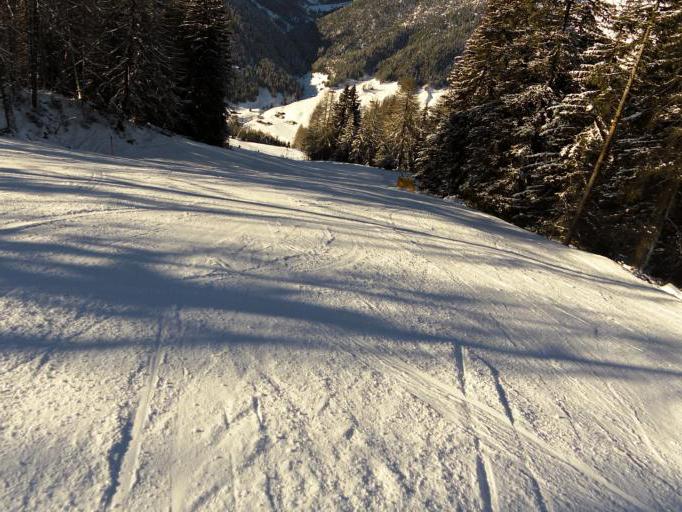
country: CH
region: Grisons
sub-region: Praettigau/Davos District
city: Davos
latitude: 46.7414
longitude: 9.7960
